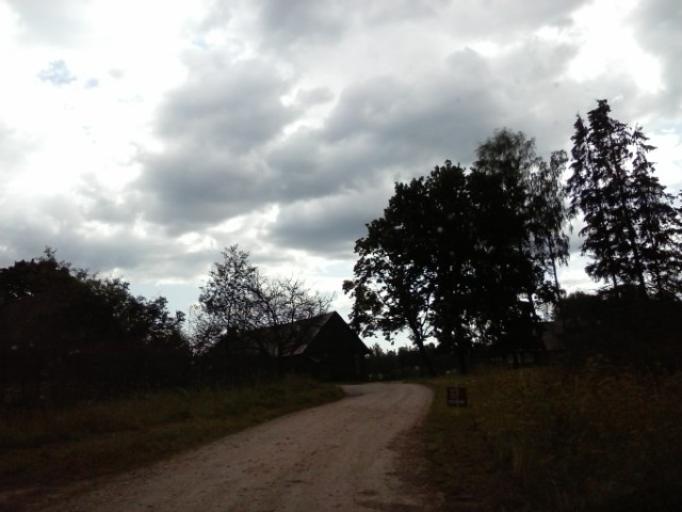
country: EE
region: Vorumaa
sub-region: Voru linn
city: Voru
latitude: 57.7474
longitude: 27.1469
